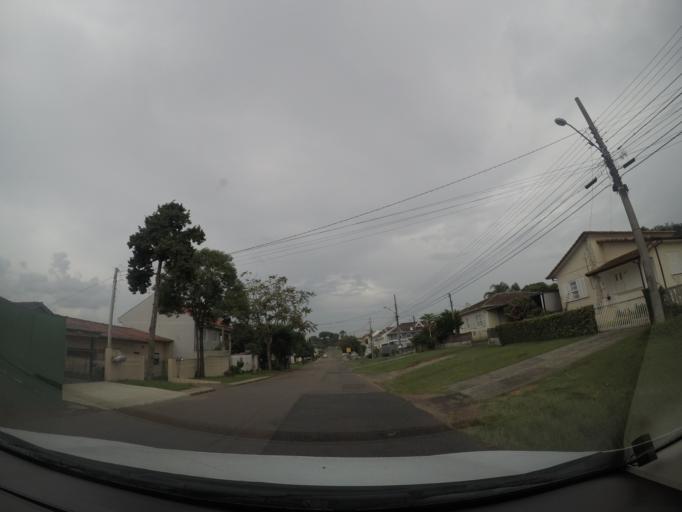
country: BR
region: Parana
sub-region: Sao Jose Dos Pinhais
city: Sao Jose dos Pinhais
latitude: -25.5094
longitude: -49.2487
